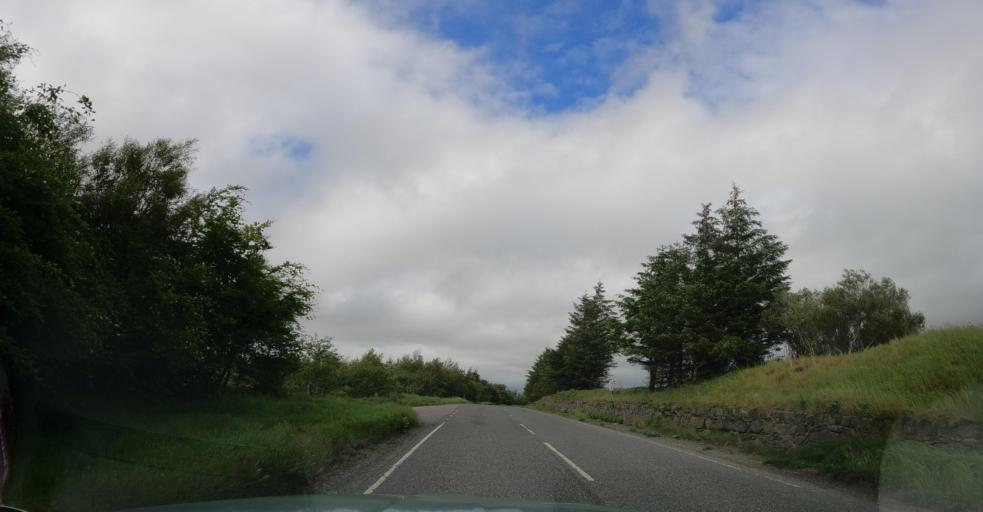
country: GB
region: Scotland
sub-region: Eilean Siar
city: Isle of Lewis
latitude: 58.2105
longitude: -6.4178
